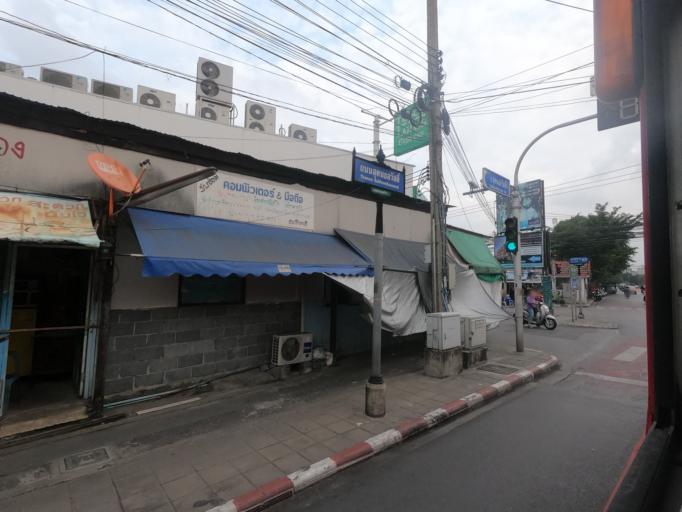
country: TH
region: Bangkok
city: Lat Phrao
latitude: 13.8214
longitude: 100.6090
